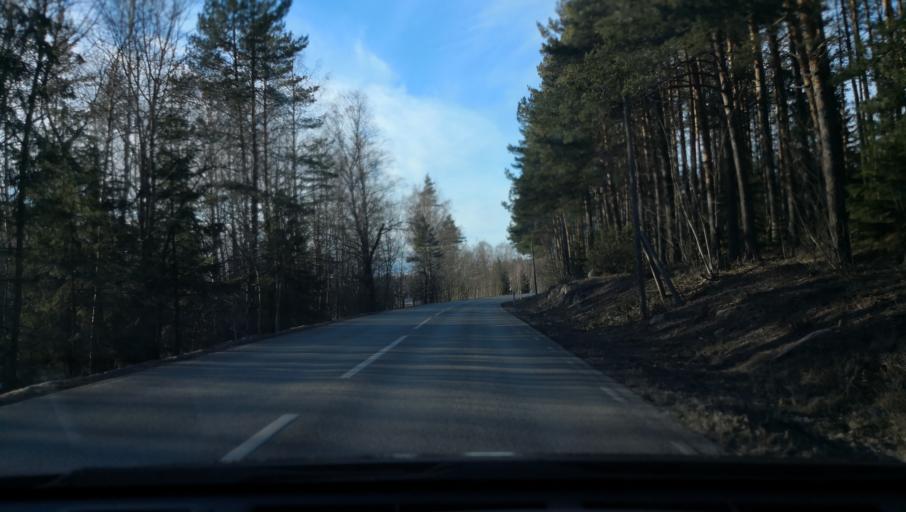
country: SE
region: Uppsala
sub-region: Osthammars Kommun
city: OEsthammar
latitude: 60.2741
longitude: 18.3085
